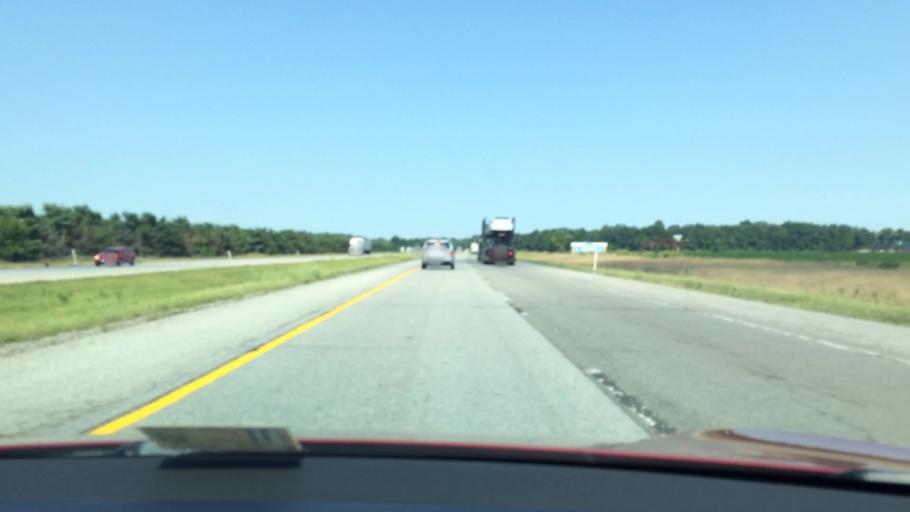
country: US
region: Michigan
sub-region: Saint Joseph County
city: White Pigeon
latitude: 41.7524
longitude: -85.6322
